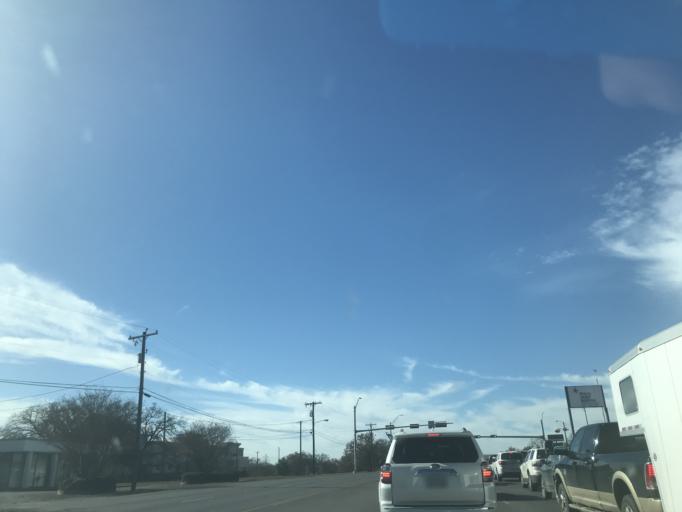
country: US
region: Texas
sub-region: Erath County
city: Stephenville
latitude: 32.2046
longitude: -98.2140
